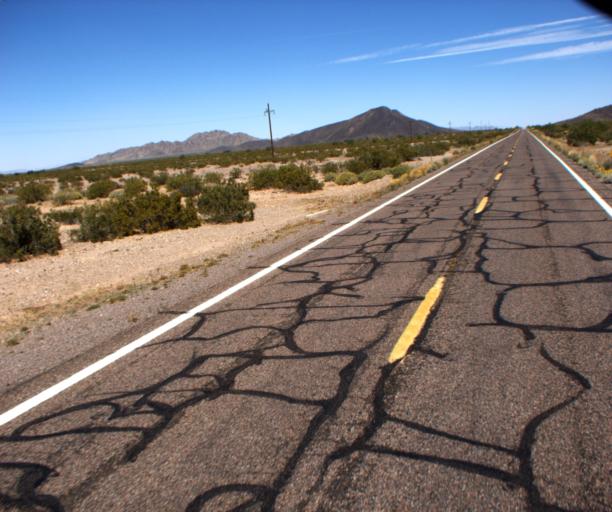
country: US
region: Arizona
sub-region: Maricopa County
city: Gila Bend
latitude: 32.7290
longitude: -112.8360
